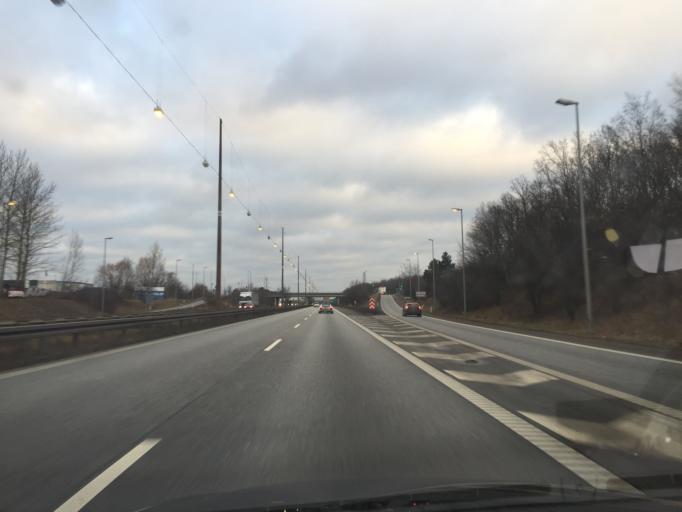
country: DK
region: Capital Region
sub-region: Ishoj Kommune
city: Ishoj
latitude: 55.6199
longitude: 12.3274
